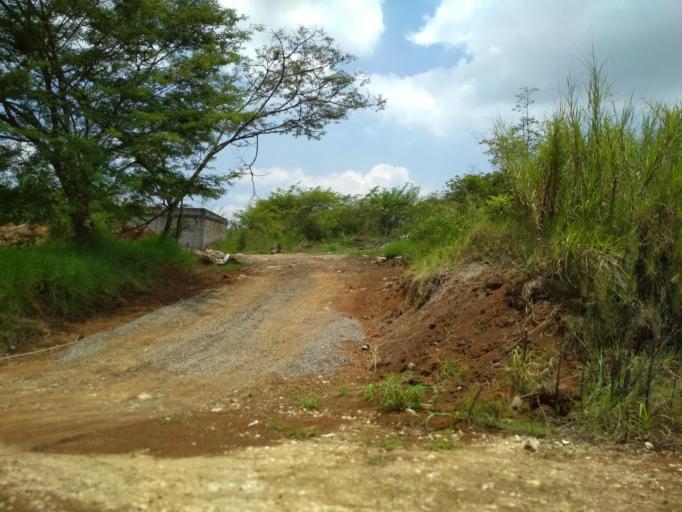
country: MX
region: Veracruz
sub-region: Ixtaczoquitlan
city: Buenavista
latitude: 18.8849
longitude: -97.0615
